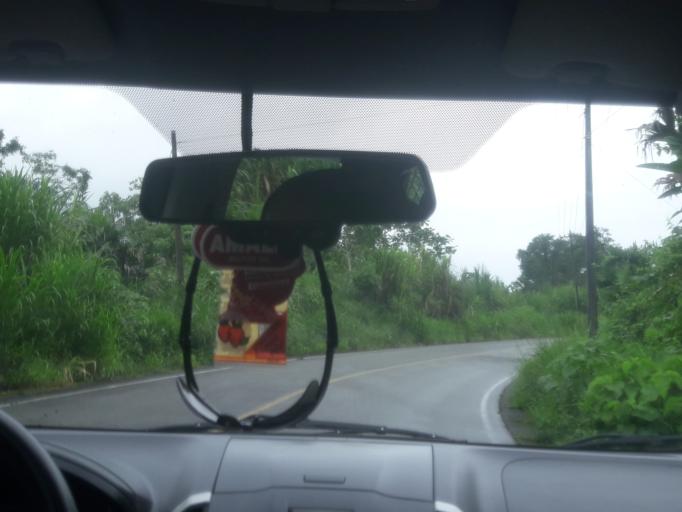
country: EC
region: Napo
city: Tena
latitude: -1.0385
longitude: -77.7128
